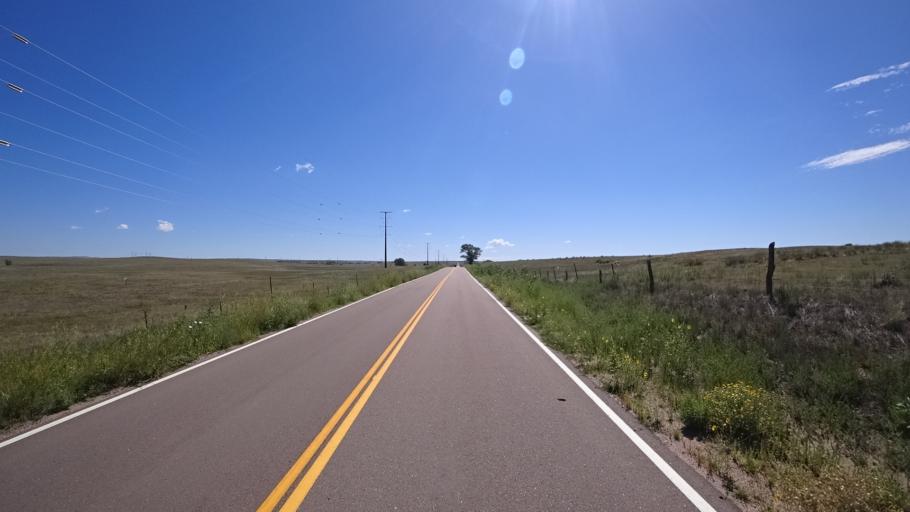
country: US
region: Colorado
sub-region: El Paso County
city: Security-Widefield
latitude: 38.7810
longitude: -104.6466
